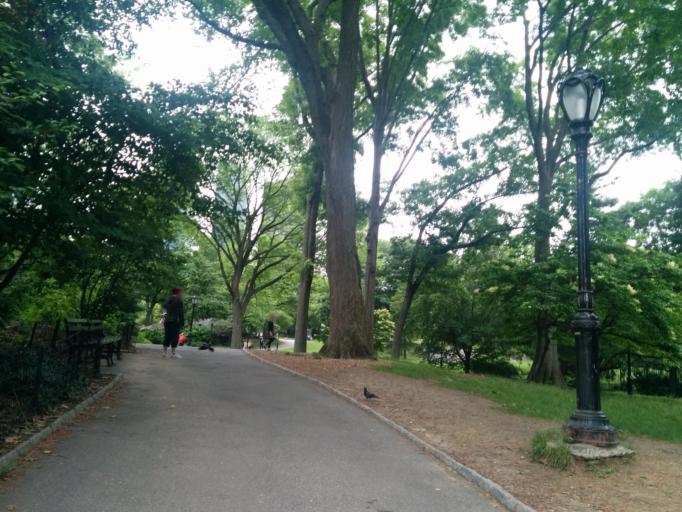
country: US
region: New York
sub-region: New York County
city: Manhattan
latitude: 40.7673
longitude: -73.9746
